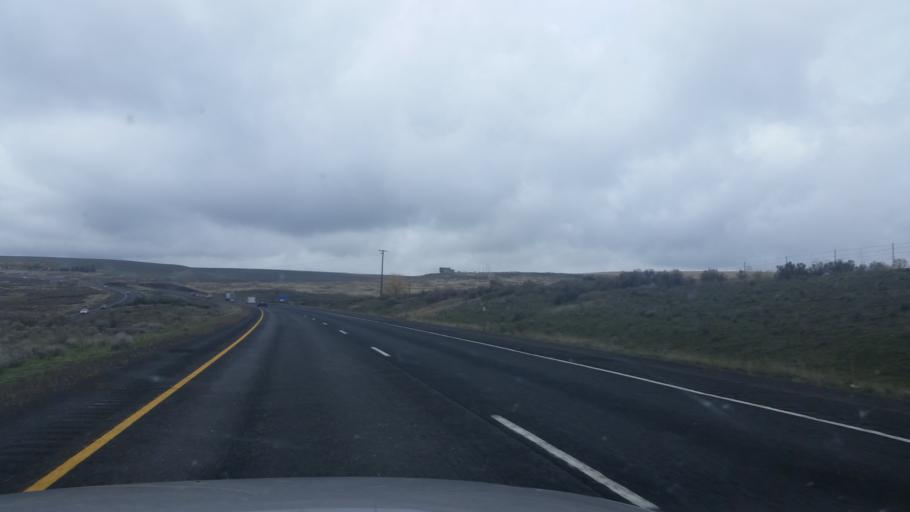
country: US
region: Washington
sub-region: Lincoln County
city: Davenport
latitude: 47.3016
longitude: -118.0125
